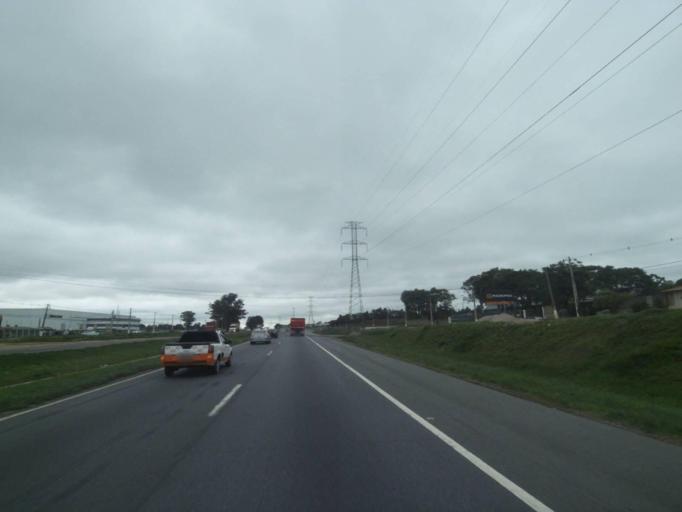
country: BR
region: Parana
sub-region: Curitiba
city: Curitiba
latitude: -25.4626
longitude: -49.3581
